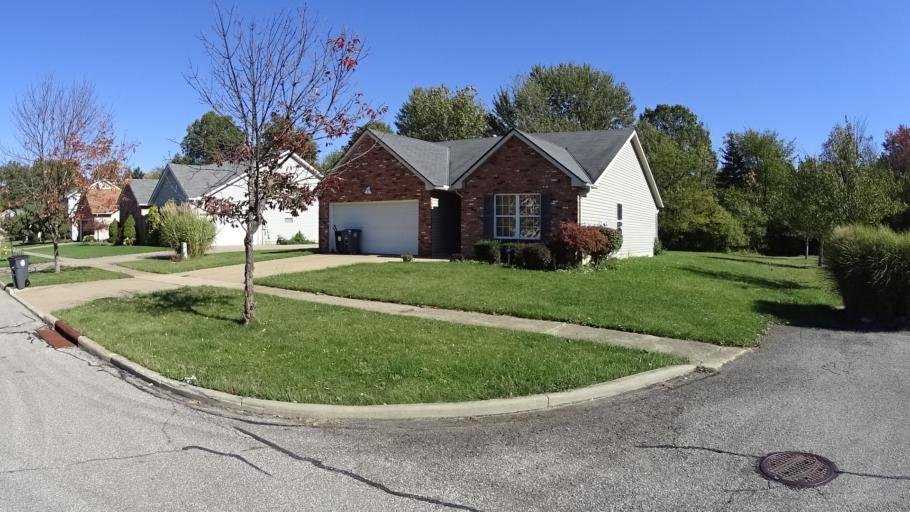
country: US
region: Ohio
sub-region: Lorain County
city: Oberlin
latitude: 41.2973
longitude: -82.2296
